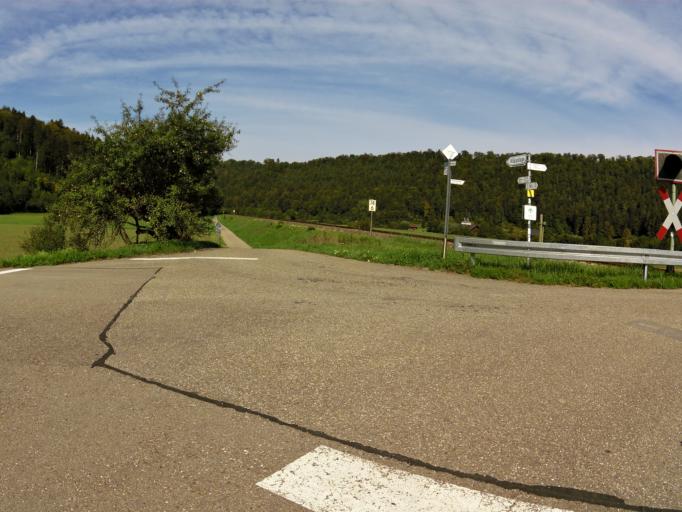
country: DE
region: Baden-Wuerttemberg
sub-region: Karlsruhe Region
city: Horb am Neckar
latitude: 48.4511
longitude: 8.7558
